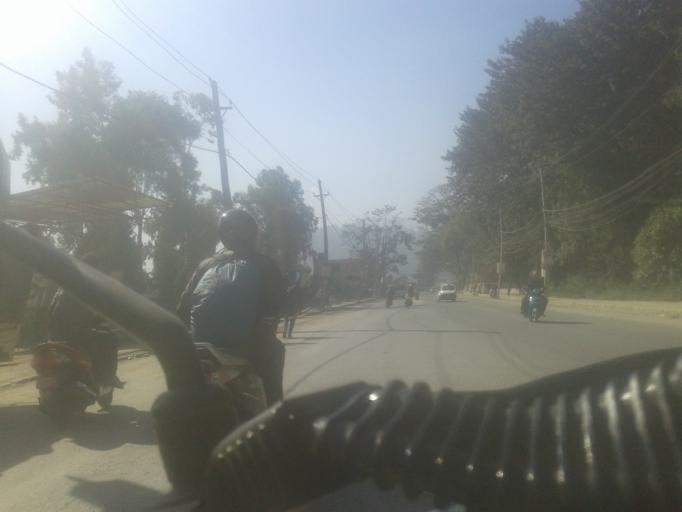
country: NP
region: Central Region
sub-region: Bagmati Zone
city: Patan
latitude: 27.6796
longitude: 85.2977
